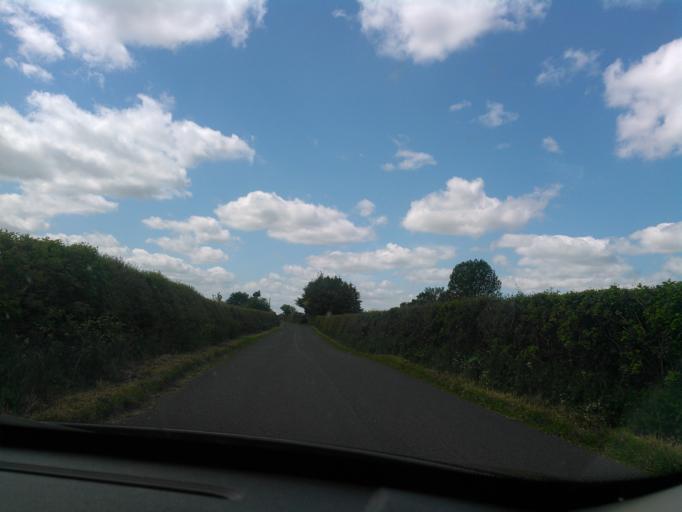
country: GB
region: England
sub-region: Shropshire
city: Prees
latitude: 52.8886
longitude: -2.6783
